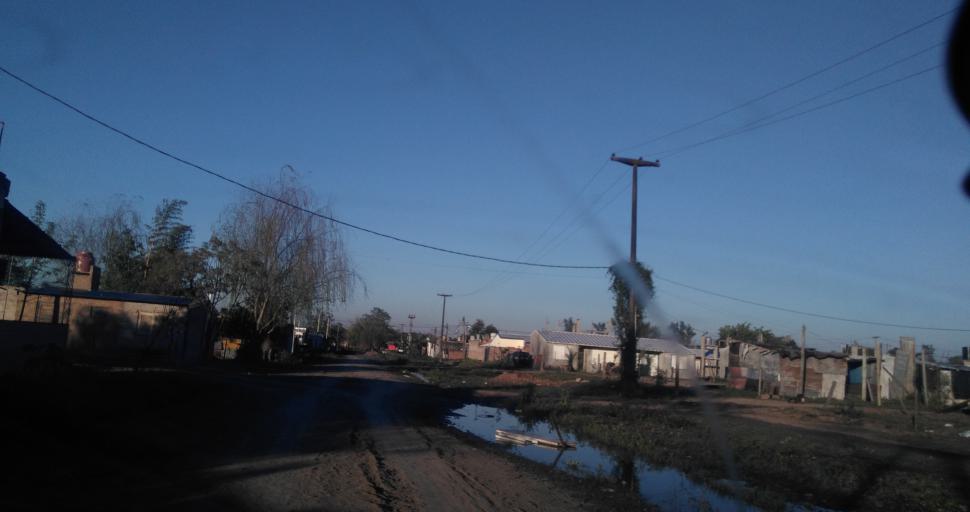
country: AR
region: Chaco
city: Fontana
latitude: -27.4211
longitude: -59.0228
